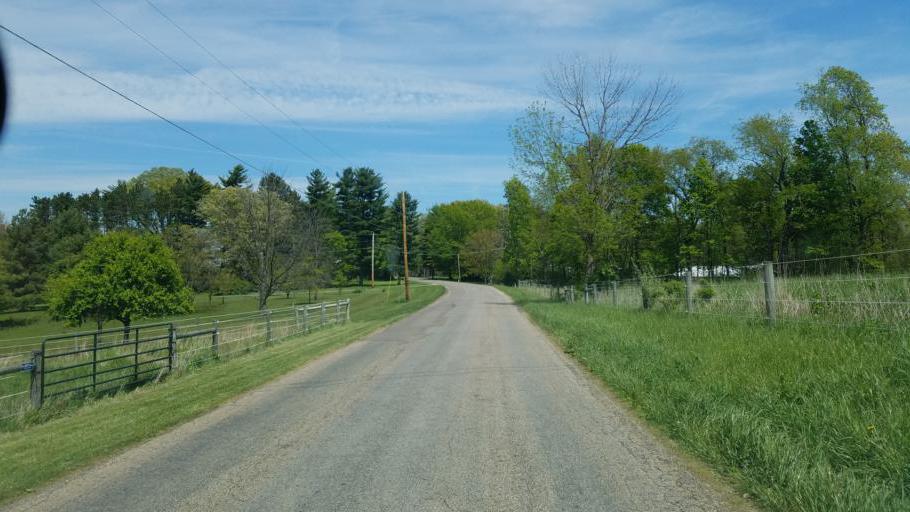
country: US
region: Ohio
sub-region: Knox County
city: Gambier
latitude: 40.4172
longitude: -82.4011
